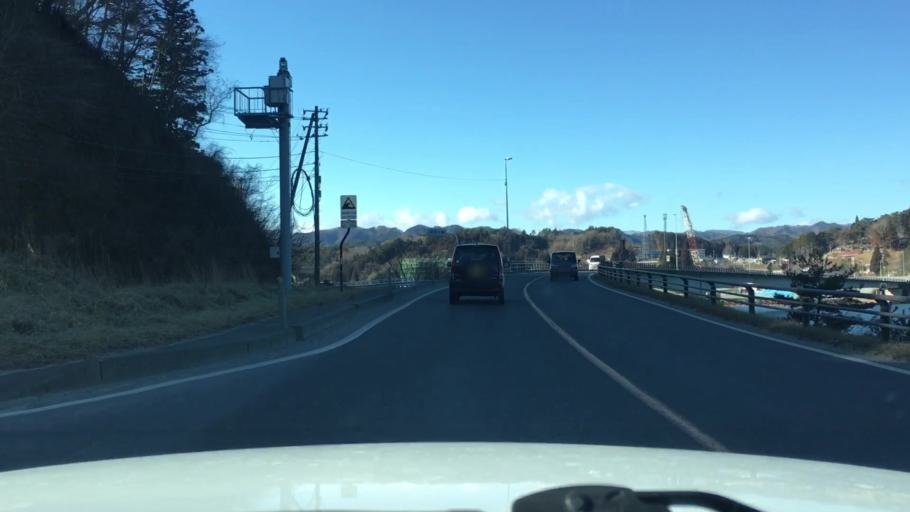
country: JP
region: Iwate
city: Yamada
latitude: 39.4477
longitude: 141.9654
